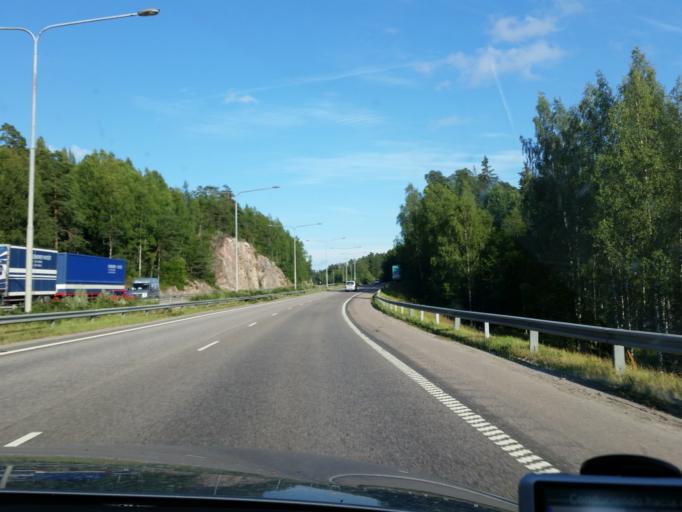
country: FI
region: Uusimaa
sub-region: Helsinki
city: Espoo
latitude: 60.2262
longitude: 24.6074
